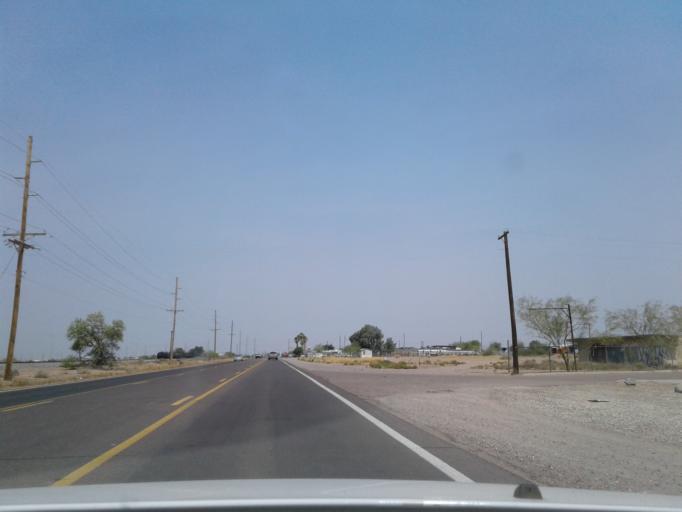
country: US
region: Arizona
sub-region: Pinal County
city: Casa Grande
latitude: 32.8614
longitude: -111.7314
